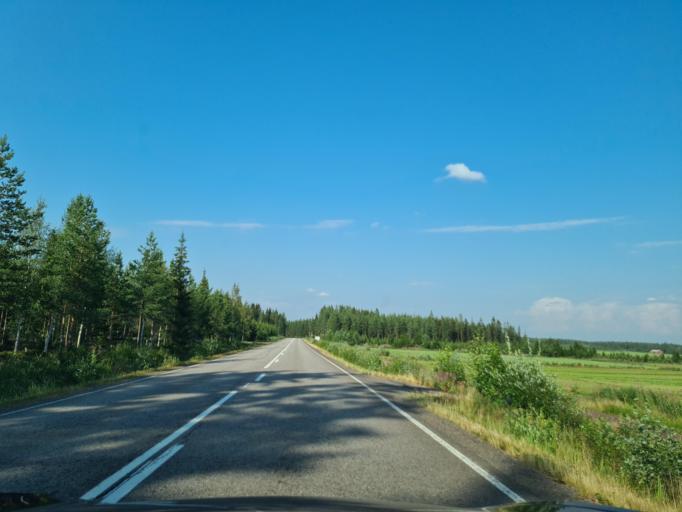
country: FI
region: Satakunta
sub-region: Pohjois-Satakunta
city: Karvia
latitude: 62.3266
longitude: 22.7036
